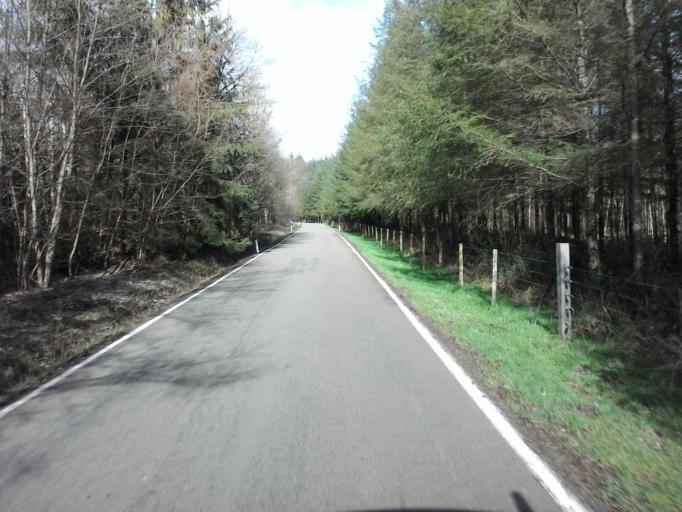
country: BE
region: Wallonia
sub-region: Province du Luxembourg
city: Daverdisse
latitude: 50.0493
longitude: 5.1340
